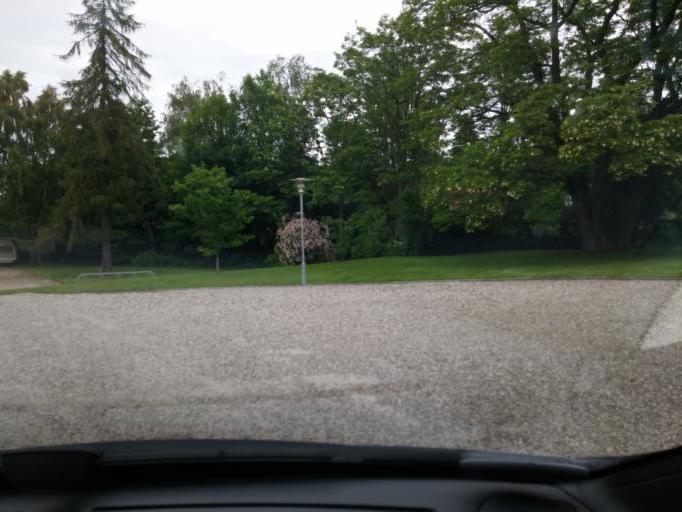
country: DK
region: Capital Region
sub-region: Hillerod Kommune
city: Hillerod
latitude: 55.9448
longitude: 12.3098
